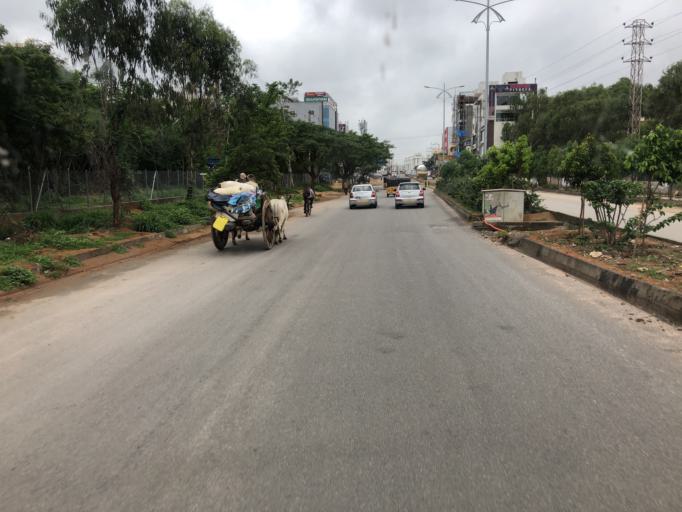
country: IN
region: Telangana
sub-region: Rangareddi
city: Kukatpalli
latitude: 17.4592
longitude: 78.3565
